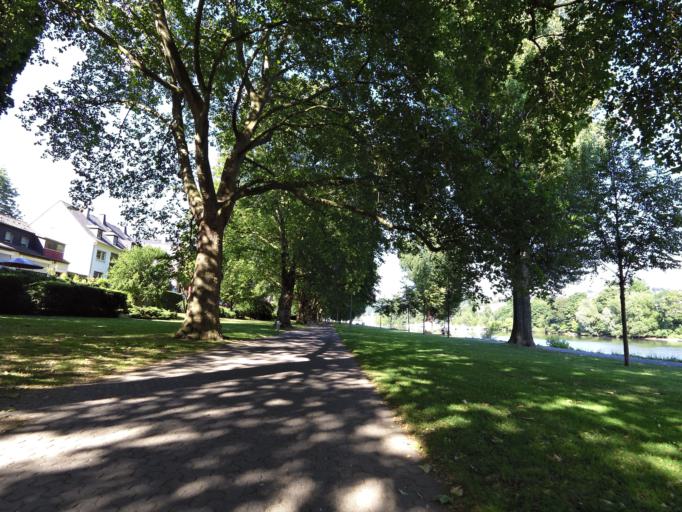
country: DE
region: Rheinland-Pfalz
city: Koblenz
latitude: 50.3434
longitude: 7.5913
